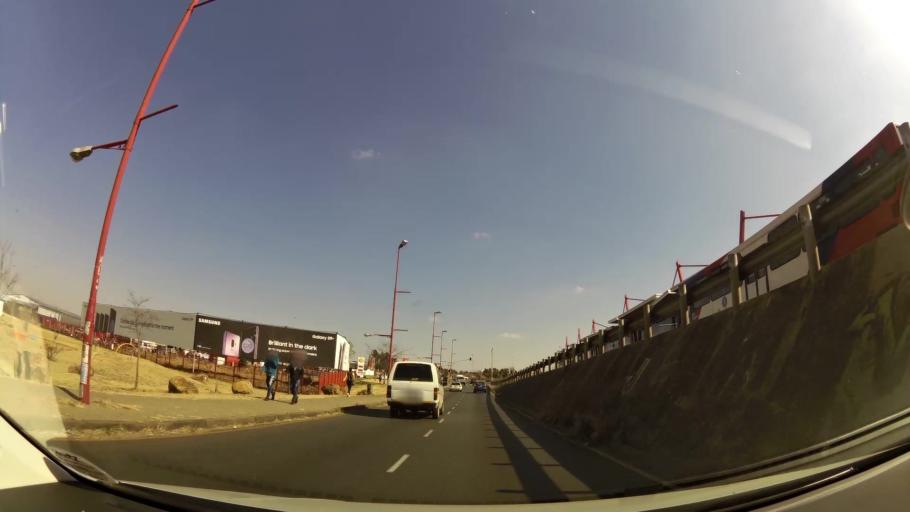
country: ZA
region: Gauteng
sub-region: City of Johannesburg Metropolitan Municipality
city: Soweto
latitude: -26.2644
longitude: 27.8804
